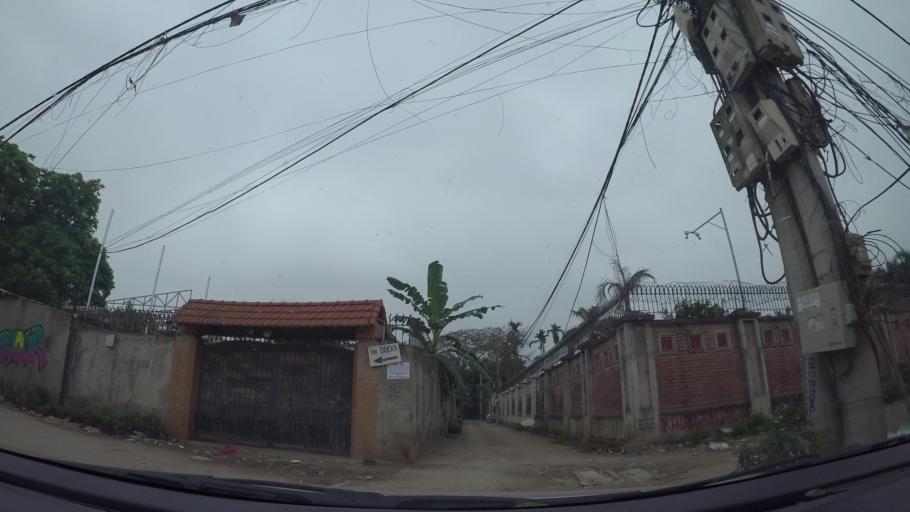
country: VN
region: Ha Noi
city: Tay Ho
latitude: 21.0712
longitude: 105.8303
